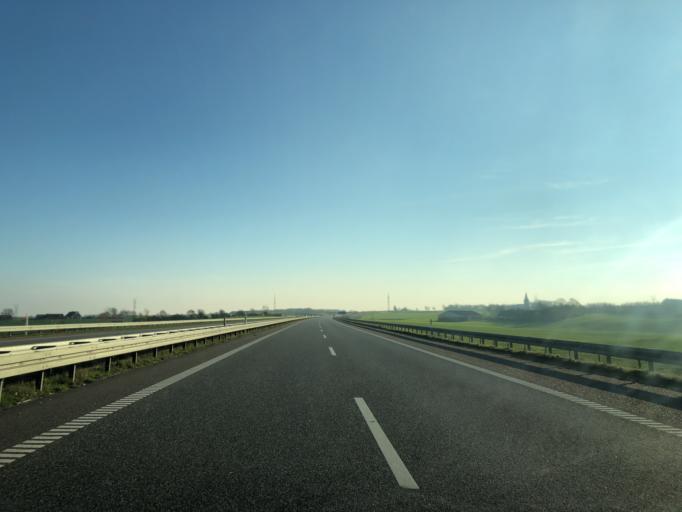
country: DK
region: Central Jutland
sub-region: Hedensted Kommune
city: Torring
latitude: 55.8116
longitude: 9.5553
